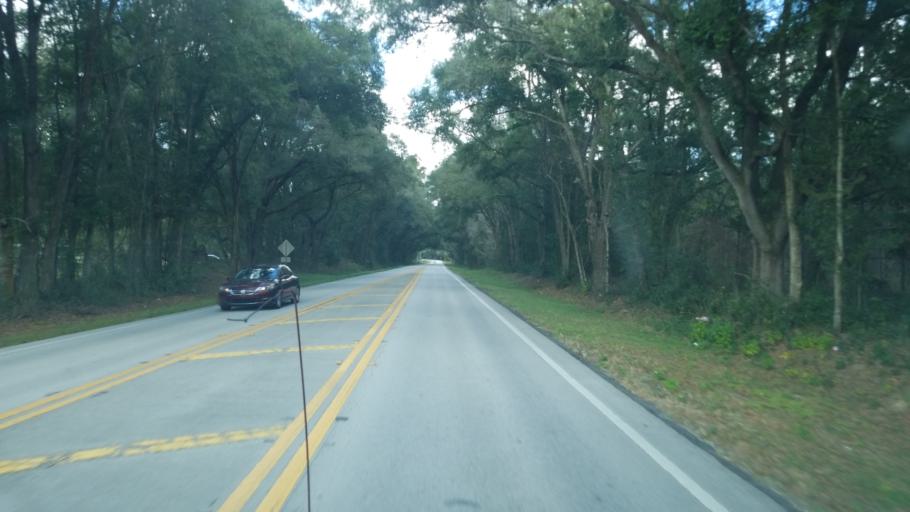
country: US
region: Florida
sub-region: Marion County
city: Belleview
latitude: 29.0594
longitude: -82.1527
